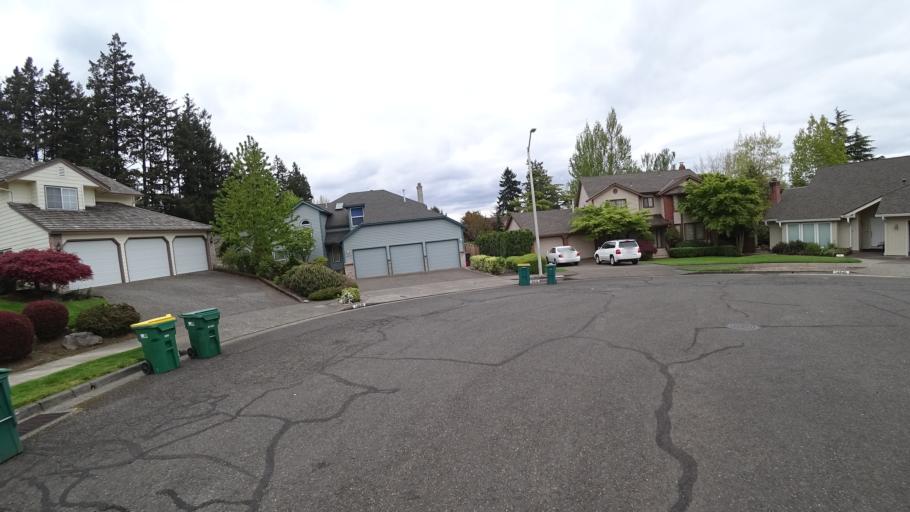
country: US
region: Oregon
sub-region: Washington County
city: Beaverton
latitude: 45.4590
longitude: -122.8216
